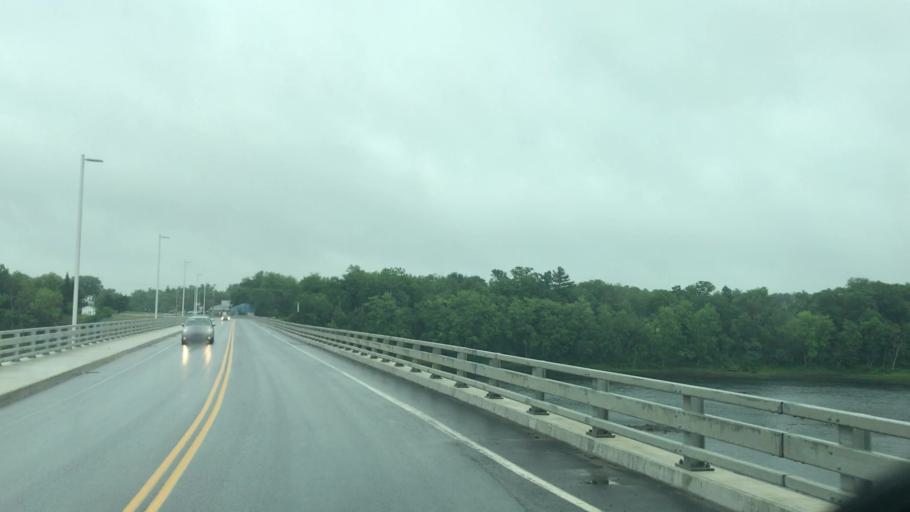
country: US
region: Maine
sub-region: Penobscot County
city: Howland
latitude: 45.2360
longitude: -68.6531
